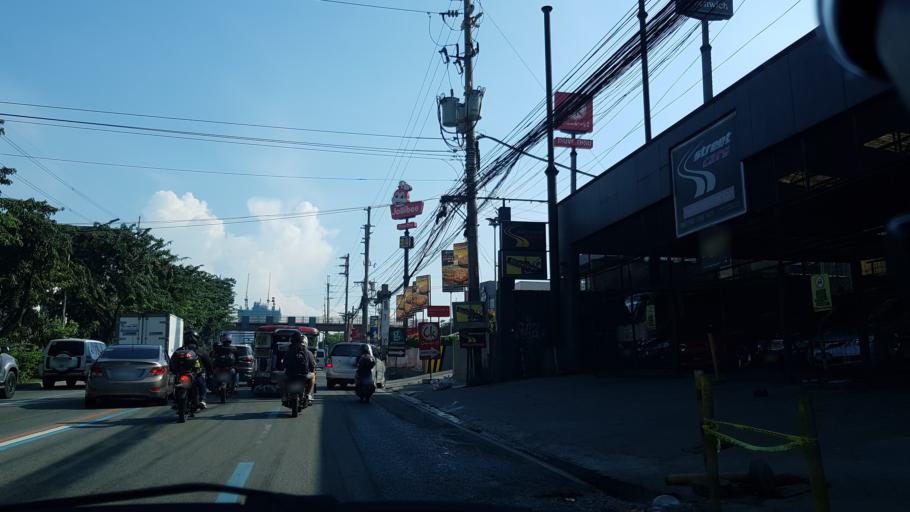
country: PH
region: Metro Manila
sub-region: Marikina
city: Calumpang
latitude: 14.6026
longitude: 121.0791
